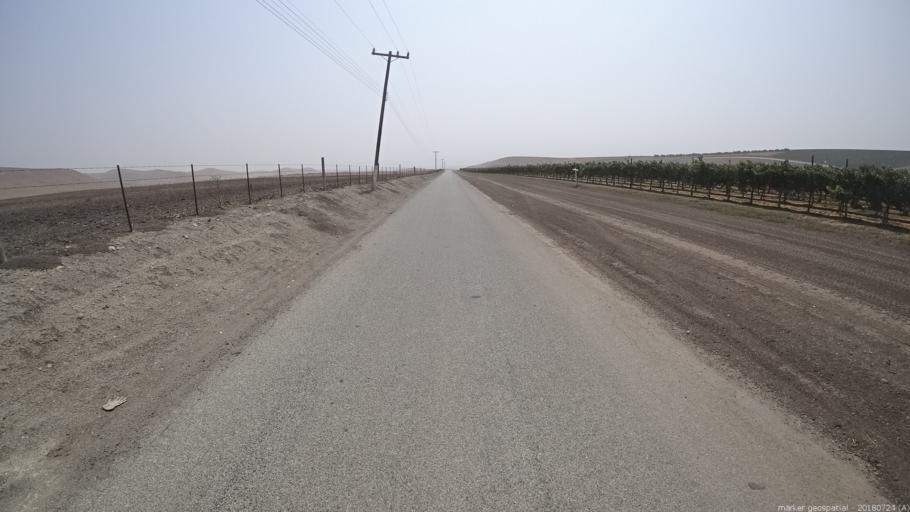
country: US
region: California
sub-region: Monterey County
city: King City
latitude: 36.1466
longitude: -121.0112
